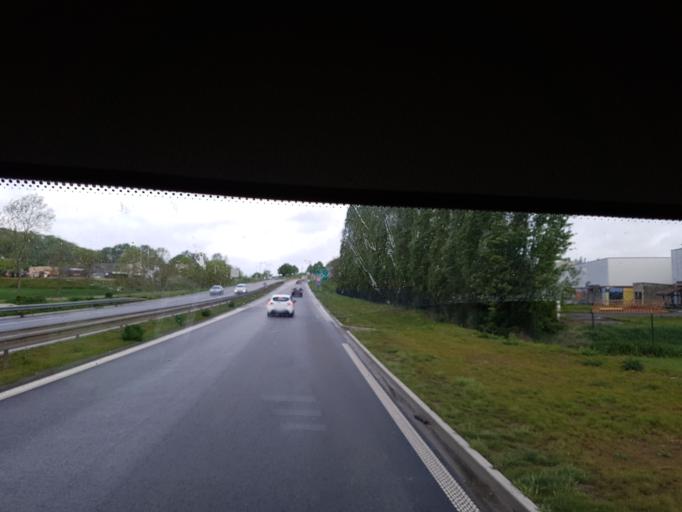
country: FR
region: Picardie
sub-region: Departement de l'Aisne
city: Courmelles
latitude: 49.3636
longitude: 3.3131
